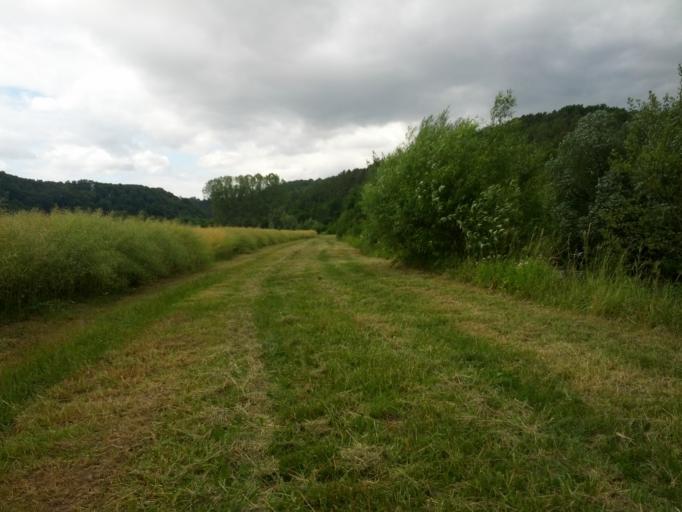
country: DE
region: Thuringia
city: Krauthausen
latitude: 50.9951
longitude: 10.2466
